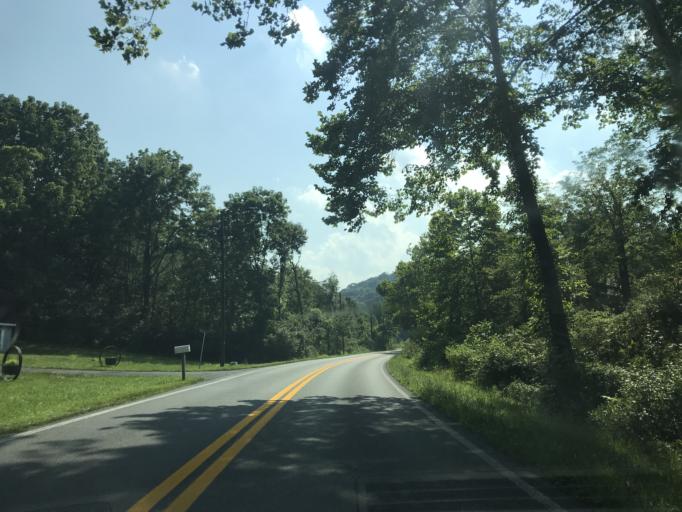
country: US
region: Maryland
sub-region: Carroll County
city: Manchester
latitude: 39.6549
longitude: -76.9266
